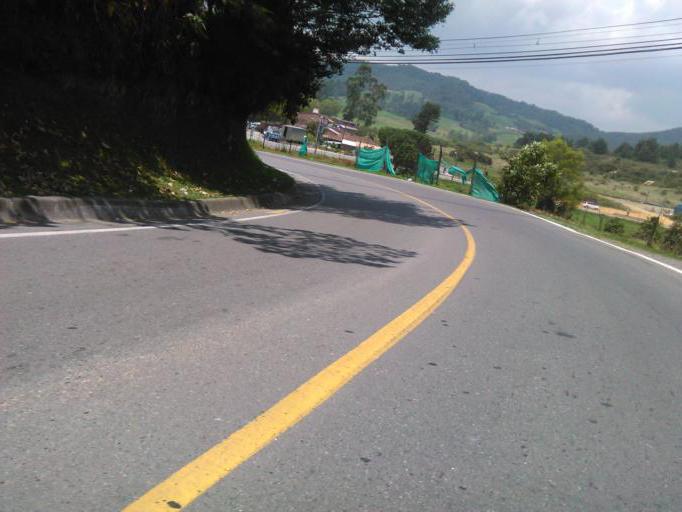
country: CO
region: Antioquia
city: La Union
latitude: 5.9828
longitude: -75.3706
